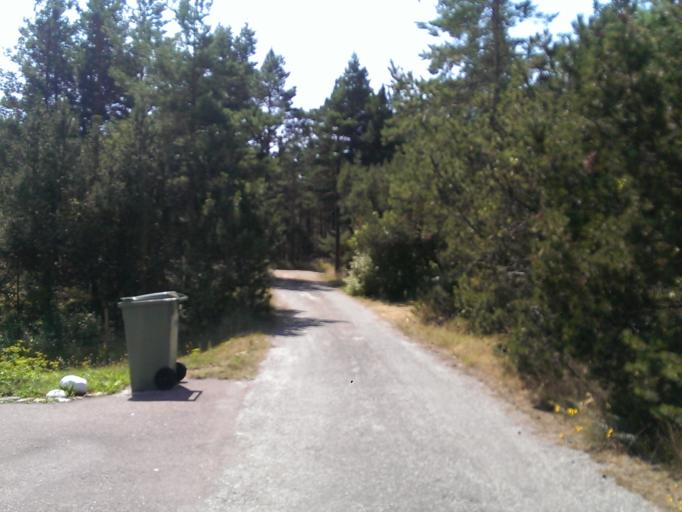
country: SE
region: Skane
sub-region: Simrishamns Kommun
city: Simrishamn
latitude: 55.4262
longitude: 14.2291
